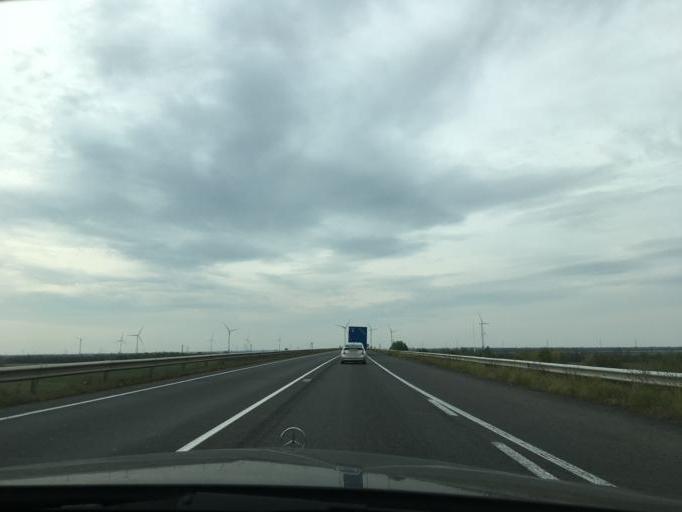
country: HU
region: Gyor-Moson-Sopron
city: Mosonmagyarovar
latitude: 47.9002
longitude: 17.1827
